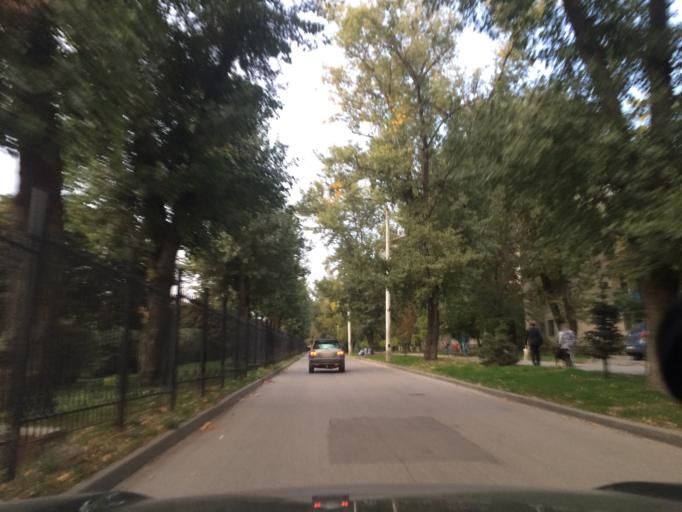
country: RU
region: Rostov
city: Rostov-na-Donu
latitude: 47.2059
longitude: 39.6339
